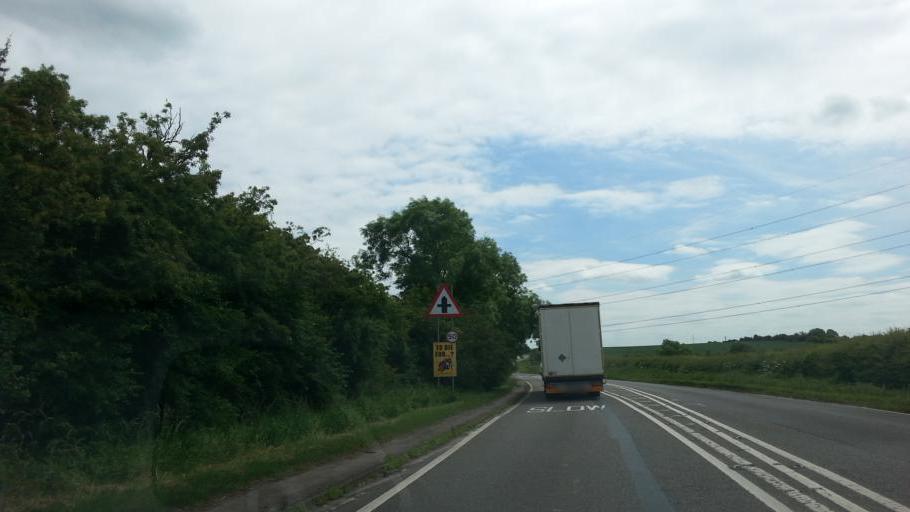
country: GB
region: England
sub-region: Nottinghamshire
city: Cotgrave
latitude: 52.8877
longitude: -1.0782
